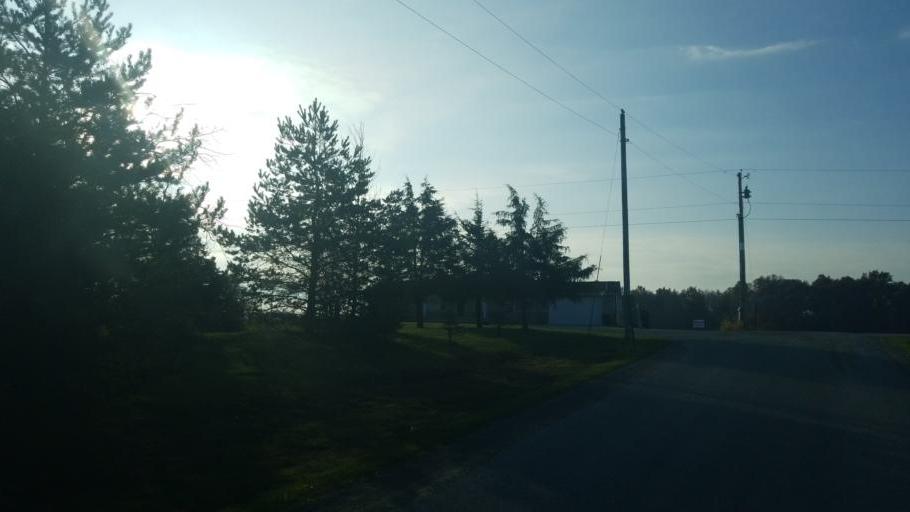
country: US
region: Ohio
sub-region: Morrow County
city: Mount Gilead
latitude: 40.5367
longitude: -82.7970
